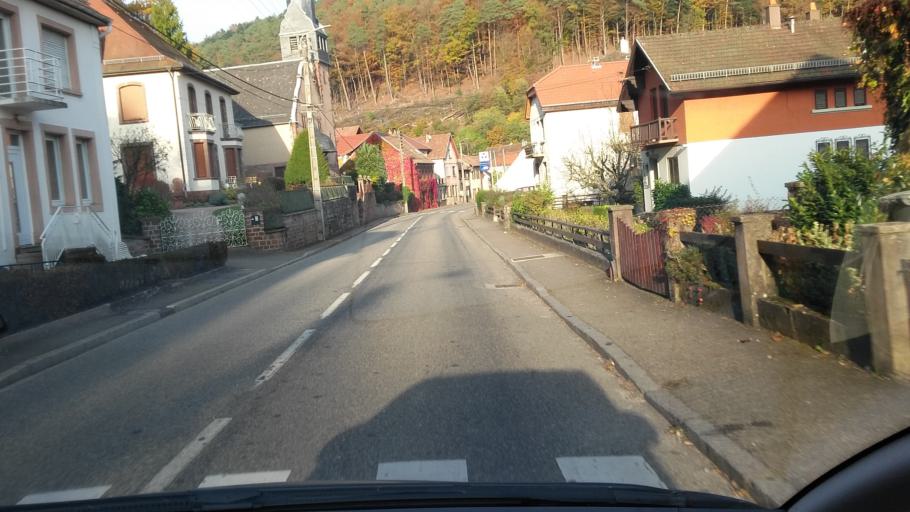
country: FR
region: Lorraine
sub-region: Departement de la Moselle
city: Phalsbourg
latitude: 48.7359
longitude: 7.2506
